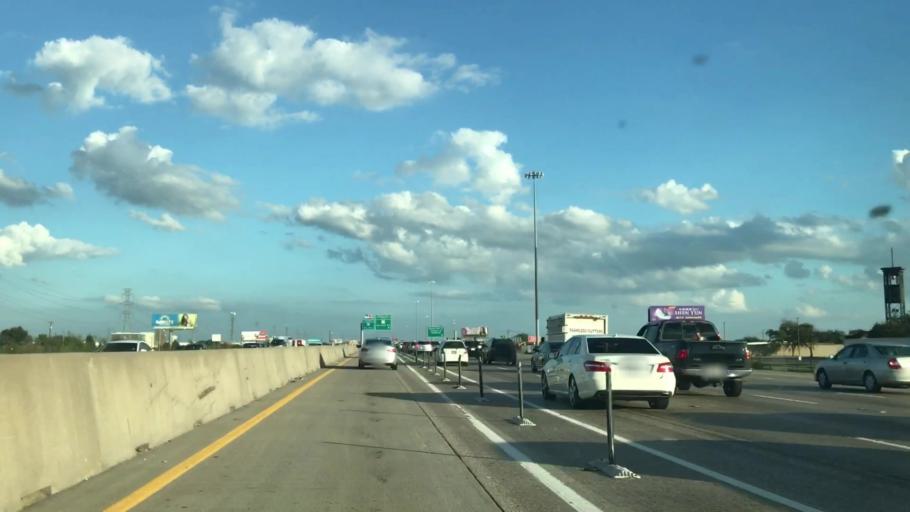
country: US
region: Texas
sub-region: Dallas County
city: Garland
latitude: 32.8825
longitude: -96.6945
